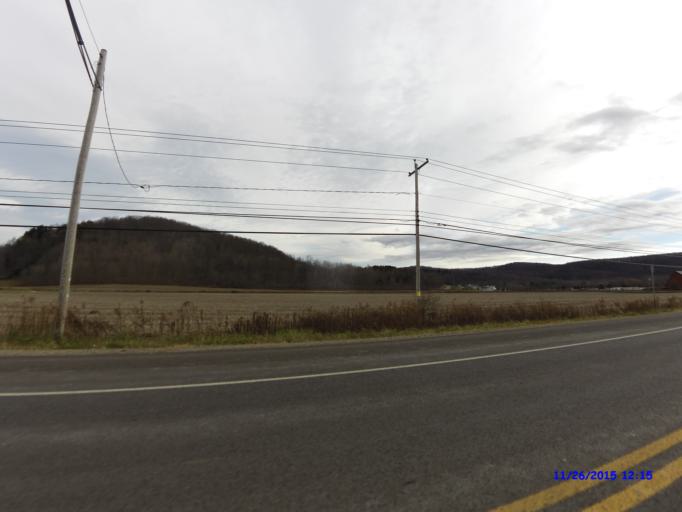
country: US
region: New York
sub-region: Cattaraugus County
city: Allegany
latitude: 42.1298
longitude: -78.5018
